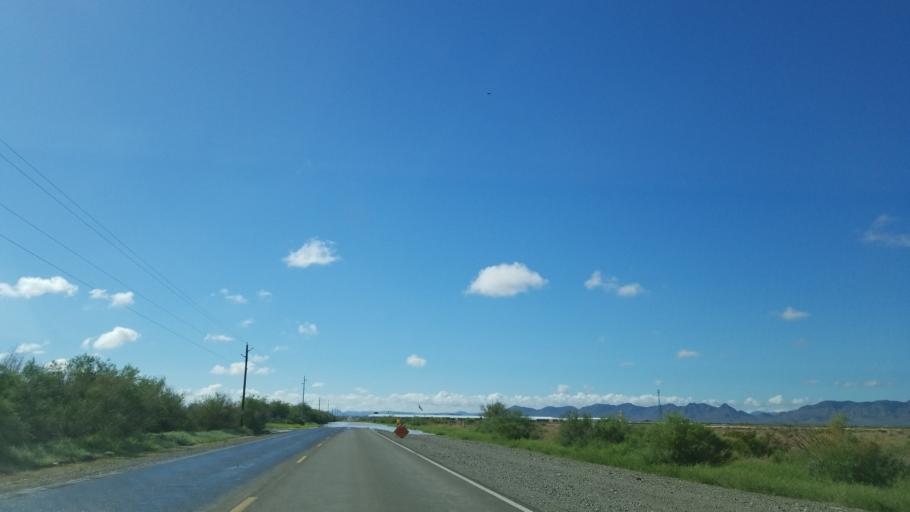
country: US
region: Arizona
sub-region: La Paz County
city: Salome
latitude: 33.6558
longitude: -113.7673
